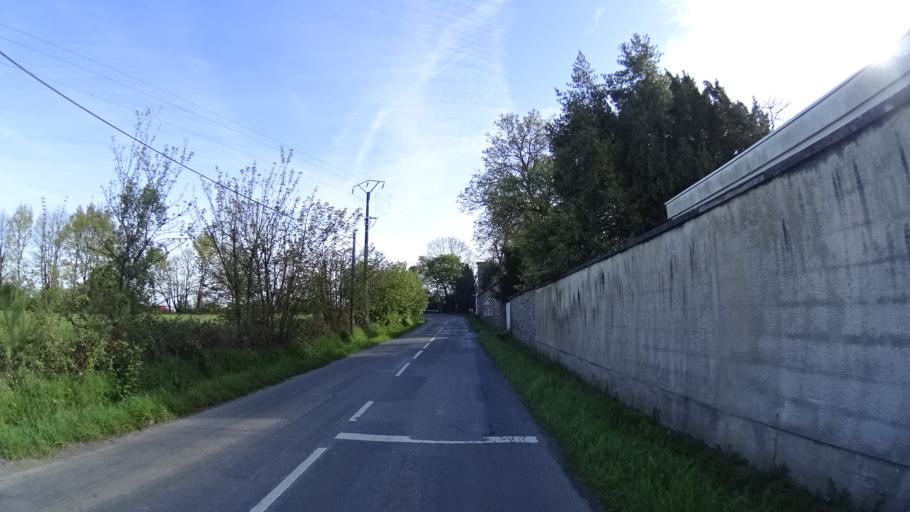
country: FR
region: Brittany
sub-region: Departement d'Ille-et-Vilaine
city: Vezin-le-Coquet
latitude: 48.1085
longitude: -1.7435
